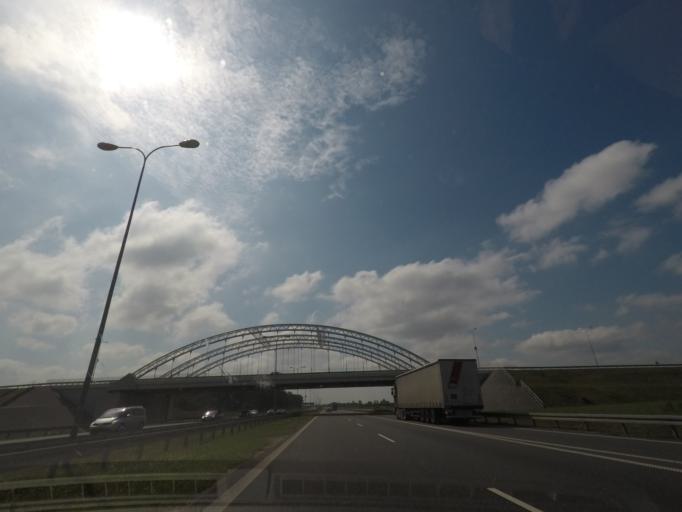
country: PL
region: Kujawsko-Pomorskie
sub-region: Powiat wloclawski
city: Lubanie
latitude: 52.6833
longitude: 18.8979
